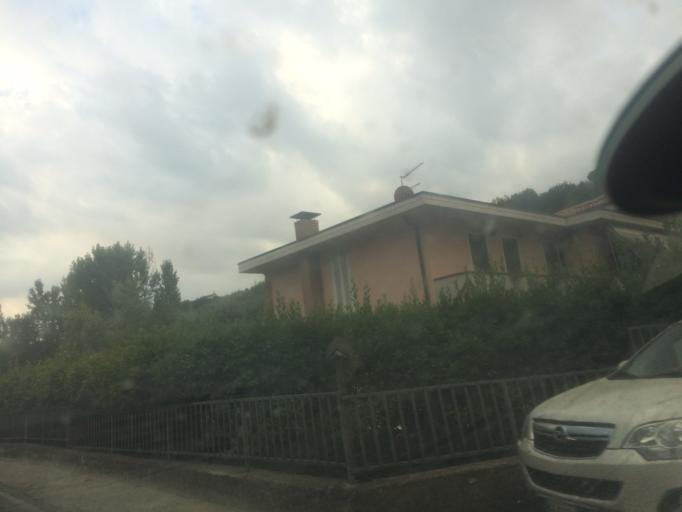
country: IT
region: Tuscany
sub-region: Provincia di Massa-Carrara
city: Carrara
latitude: 44.0598
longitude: 10.0791
